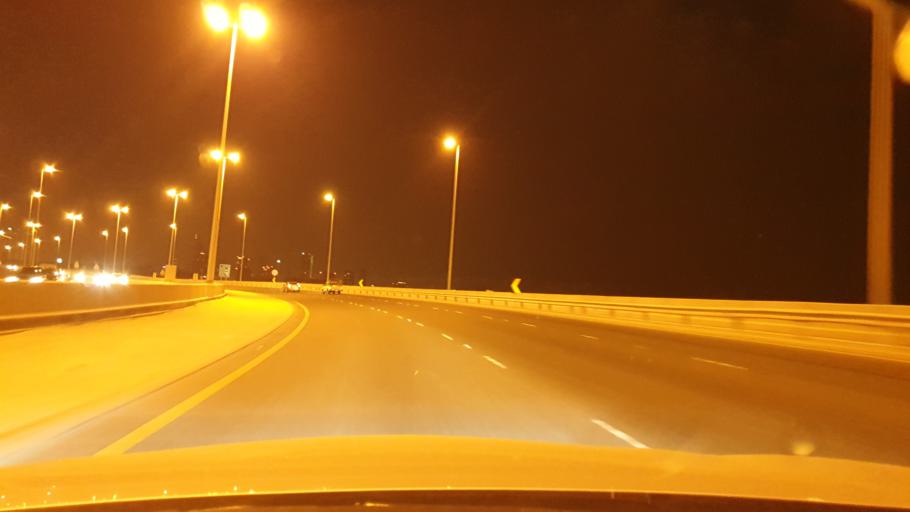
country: BH
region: Muharraq
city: Al Muharraq
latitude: 26.2532
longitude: 50.5784
